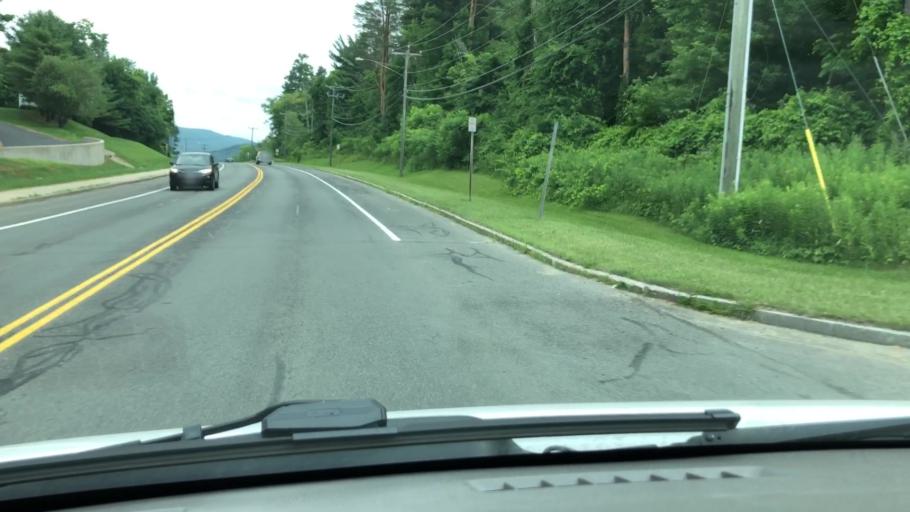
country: US
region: Massachusetts
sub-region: Berkshire County
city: Pittsfield
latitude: 42.4854
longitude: -73.2459
